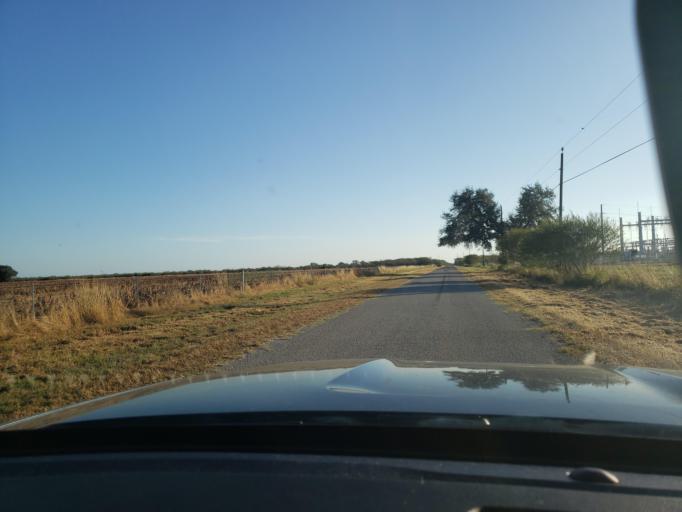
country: US
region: Texas
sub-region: Bee County
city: Beeville
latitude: 28.4306
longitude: -97.6903
